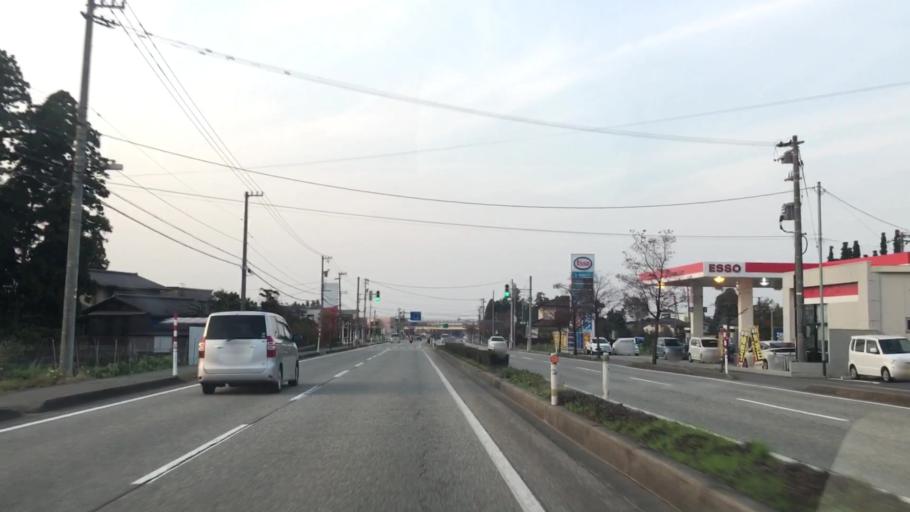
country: JP
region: Toyama
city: Toyama-shi
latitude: 36.6424
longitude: 137.2363
